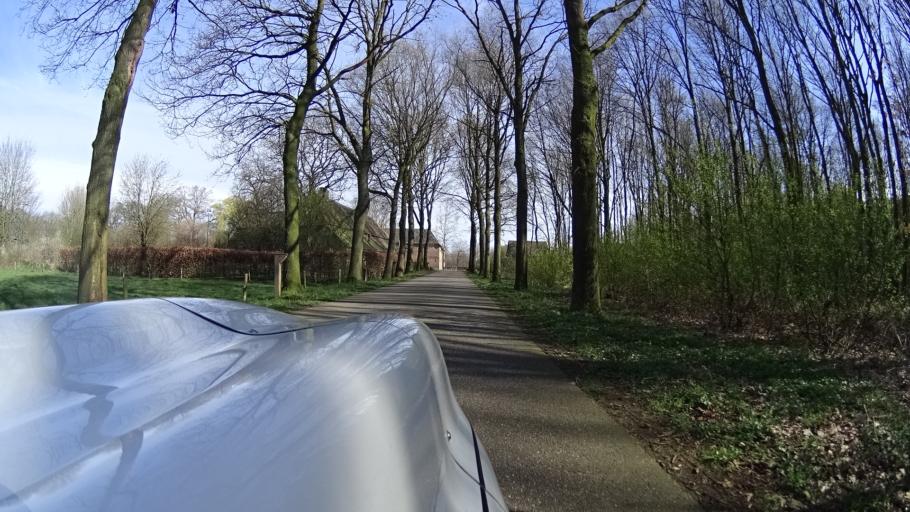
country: NL
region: North Brabant
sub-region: Gemeente Mill en Sint Hubert
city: Wilbertoord
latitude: 51.7119
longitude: 5.7797
